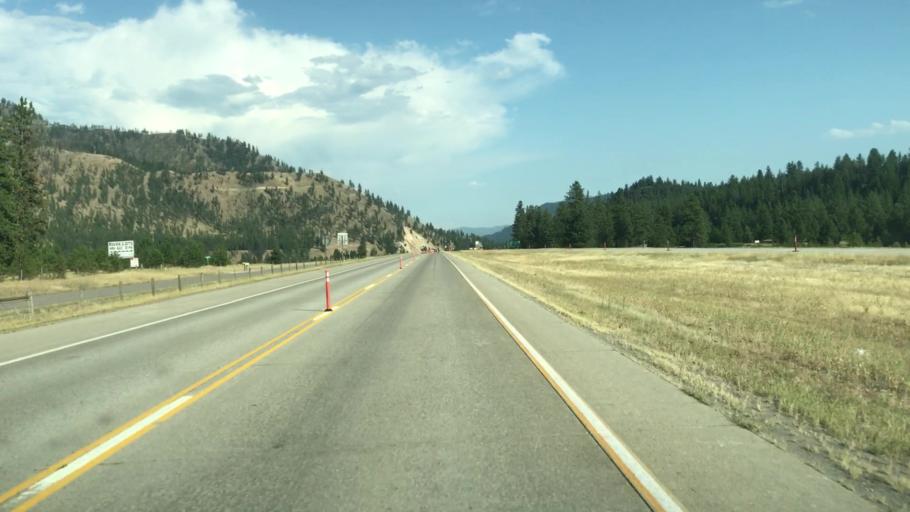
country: US
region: Montana
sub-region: Mineral County
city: Superior
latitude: 47.2311
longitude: -114.9802
